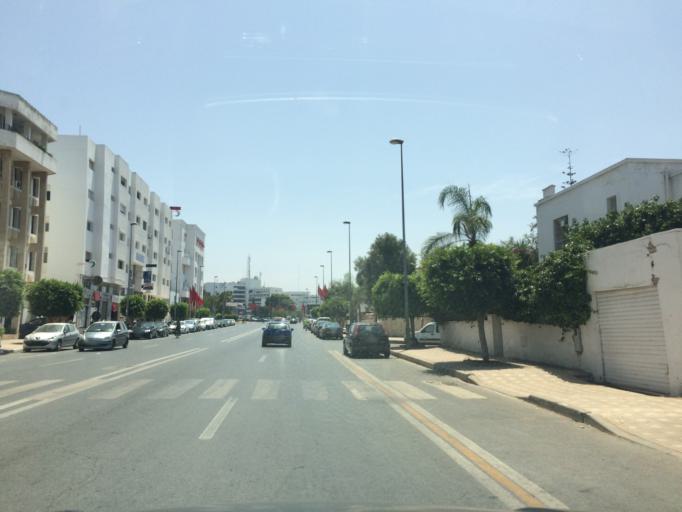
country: MA
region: Rabat-Sale-Zemmour-Zaer
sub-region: Rabat
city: Rabat
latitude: 33.9889
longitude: -6.8515
